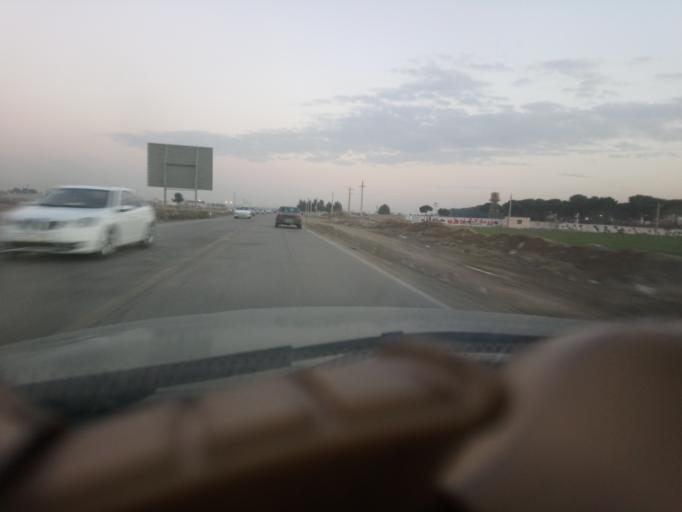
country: IR
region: Tehran
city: Shahrak-e Emam Hasan-e Mojtaba
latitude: 35.5058
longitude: 51.3287
